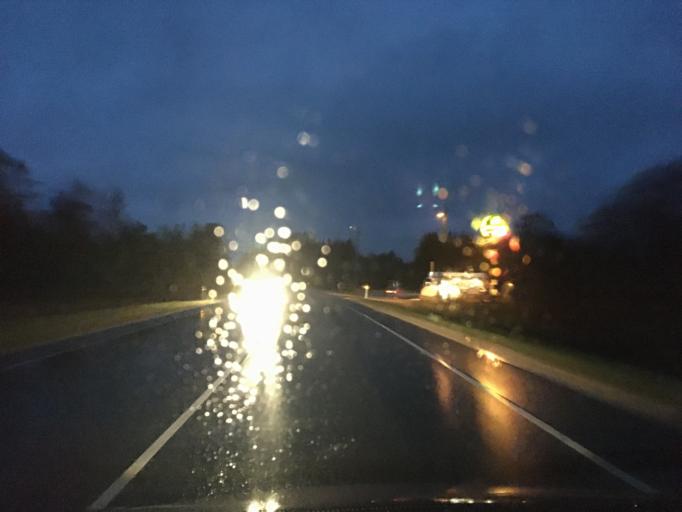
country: EE
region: Harju
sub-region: Nissi vald
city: Turba
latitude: 59.0618
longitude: 24.1939
